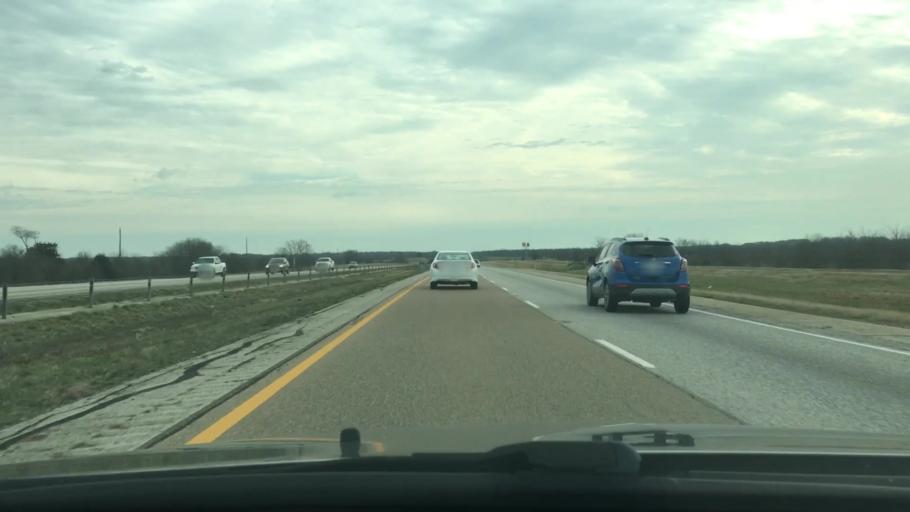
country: US
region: Texas
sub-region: Leon County
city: Centerville
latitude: 31.1037
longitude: -95.9650
